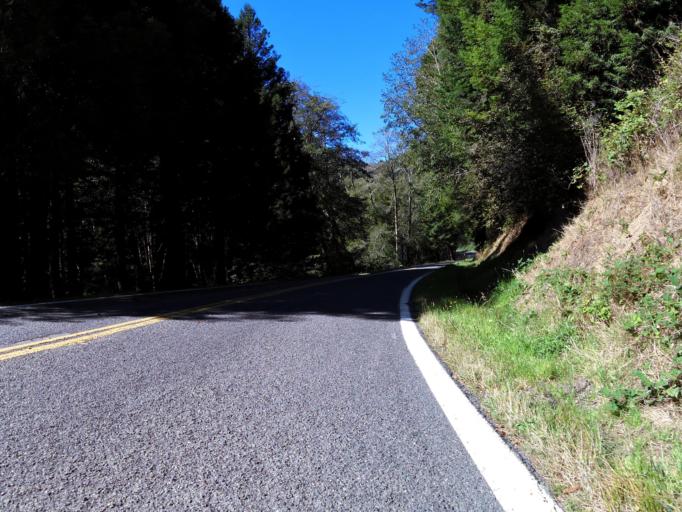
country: US
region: California
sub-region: Mendocino County
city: Fort Bragg
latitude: 39.7799
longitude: -123.8259
